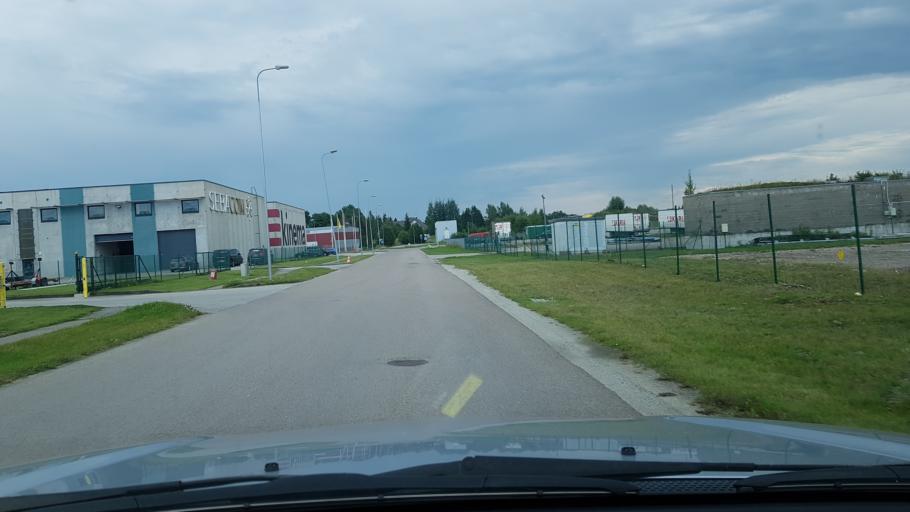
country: EE
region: Harju
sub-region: Rae vald
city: Jueri
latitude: 59.3489
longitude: 24.8943
